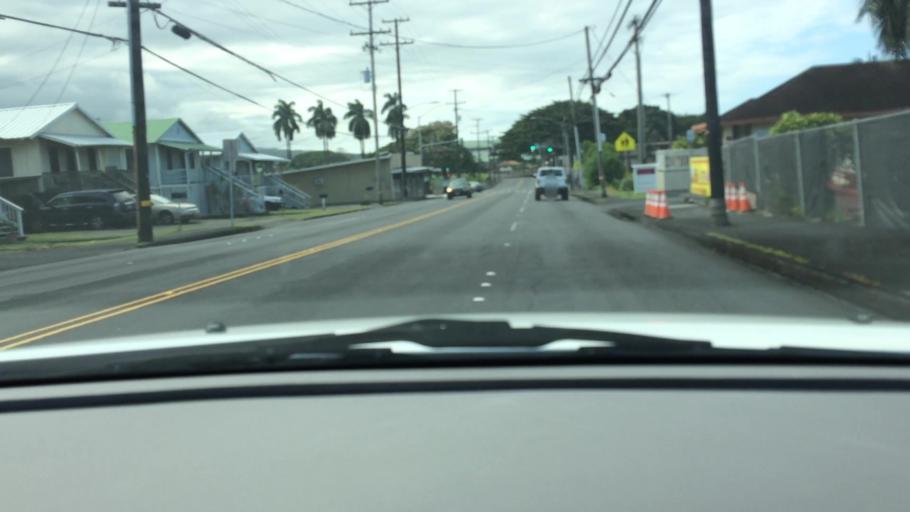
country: US
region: Hawaii
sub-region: Hawaii County
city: Hilo
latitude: 19.7126
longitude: -155.0772
